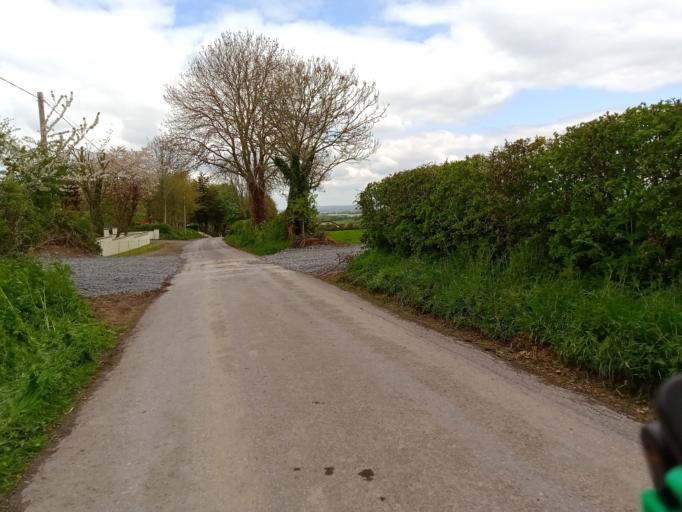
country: IE
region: Leinster
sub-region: Kilkenny
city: Kilkenny
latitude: 52.6215
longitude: -7.2385
